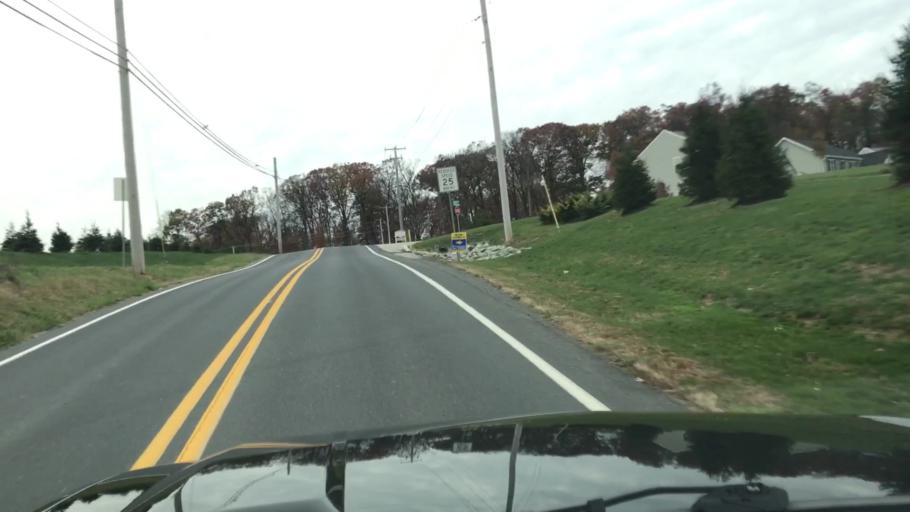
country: US
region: Pennsylvania
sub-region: Cumberland County
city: Shiremanstown
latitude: 40.1929
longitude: -76.9610
